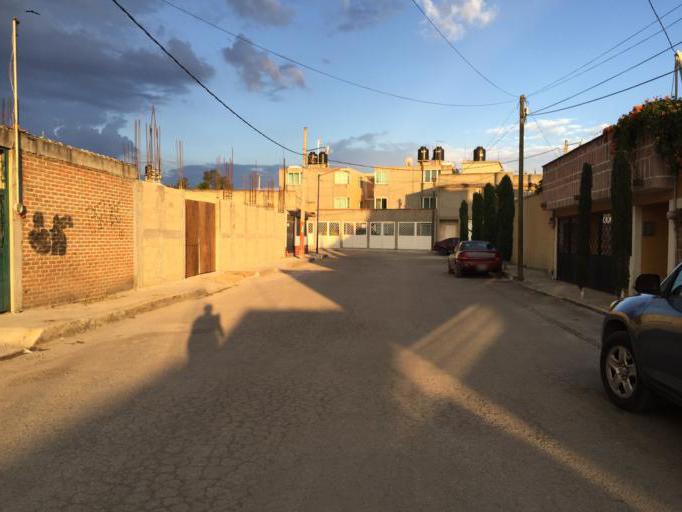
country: MX
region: Mexico
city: Cuautitlan Izcalli
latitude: 19.6657
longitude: -99.2194
